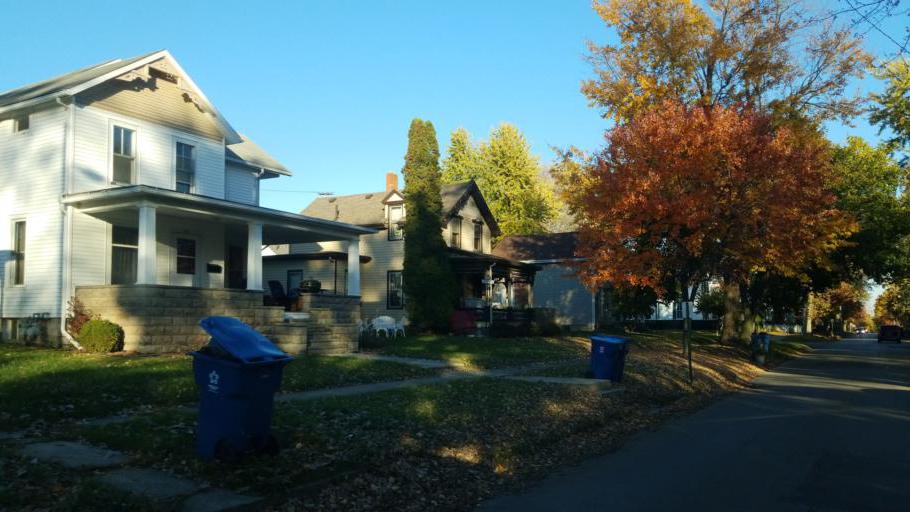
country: US
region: Ohio
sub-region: Sandusky County
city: Fremont
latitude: 41.3443
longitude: -83.1207
